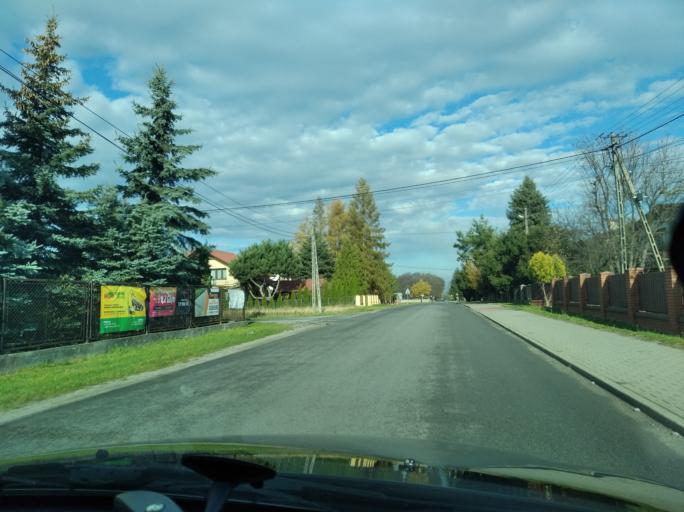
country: PL
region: Subcarpathian Voivodeship
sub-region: Powiat debicki
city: Brzeznica
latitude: 50.0530
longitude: 21.4842
